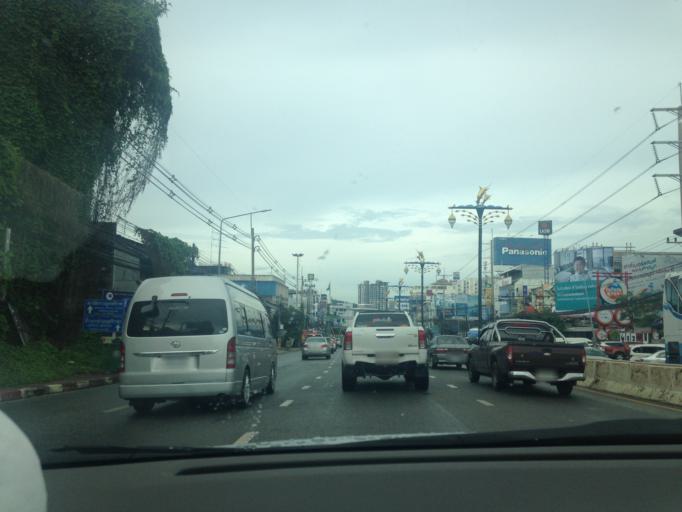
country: TH
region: Chon Buri
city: Si Racha
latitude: 13.1624
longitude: 100.9277
